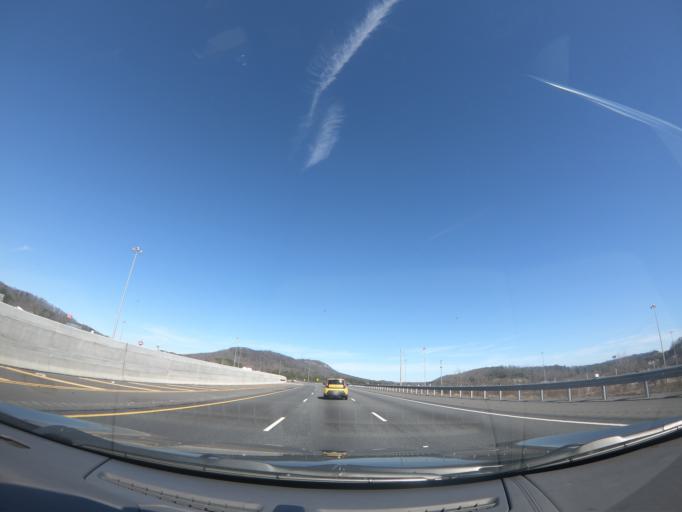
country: US
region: Georgia
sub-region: Whitfield County
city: Dalton
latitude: 34.7925
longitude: -85.0007
